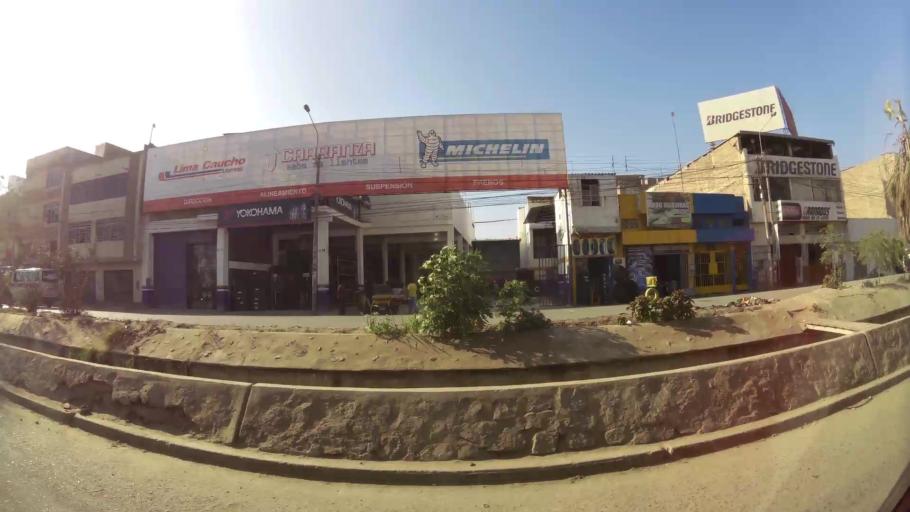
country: PE
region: Lambayeque
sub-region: Provincia de Chiclayo
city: Chiclayo
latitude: -6.7622
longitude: -79.8438
